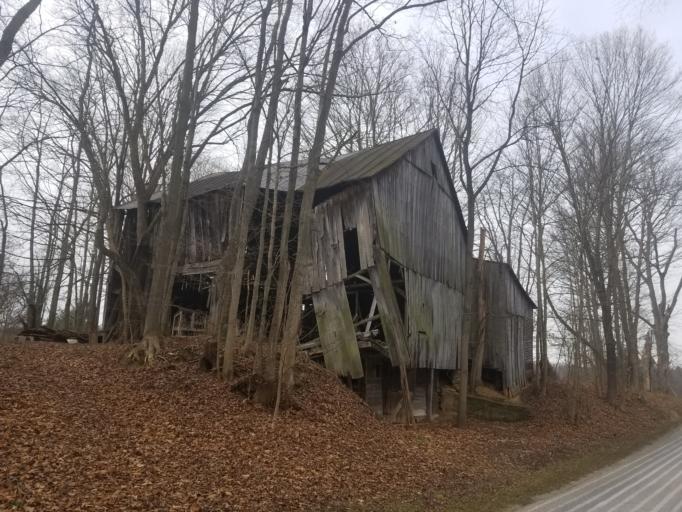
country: US
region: Ohio
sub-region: Sandusky County
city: Bellville
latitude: 40.6300
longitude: -82.5440
